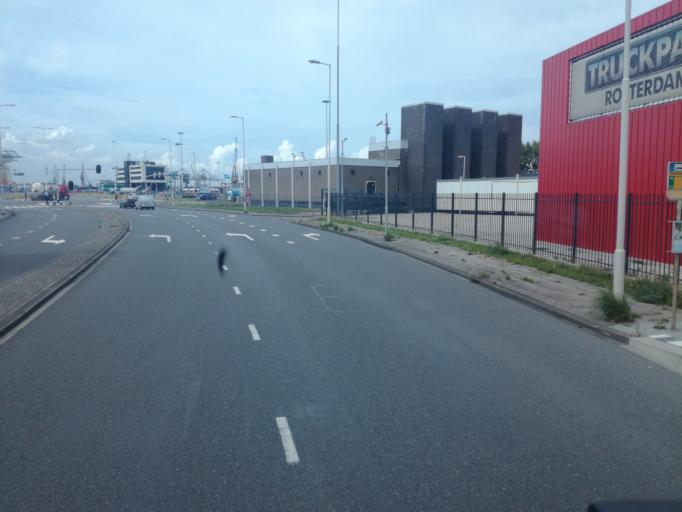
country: NL
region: South Holland
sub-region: Gemeente Albrandswaard
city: Rhoon
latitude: 51.8753
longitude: 4.4332
